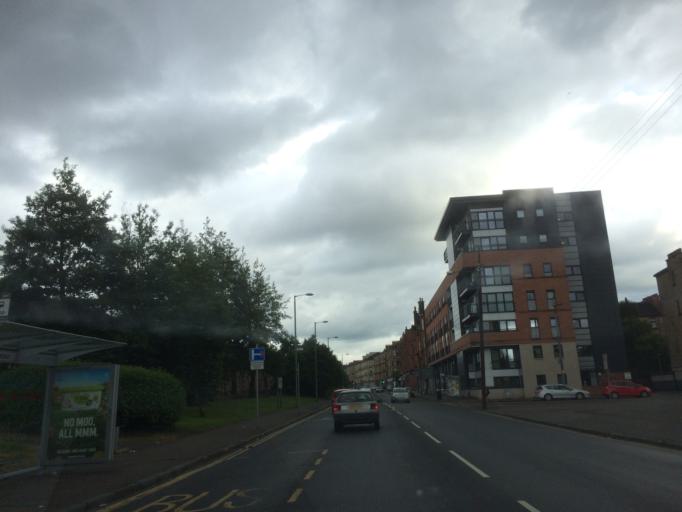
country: GB
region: Scotland
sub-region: Glasgow City
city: Glasgow
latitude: 55.8405
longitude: -4.2563
